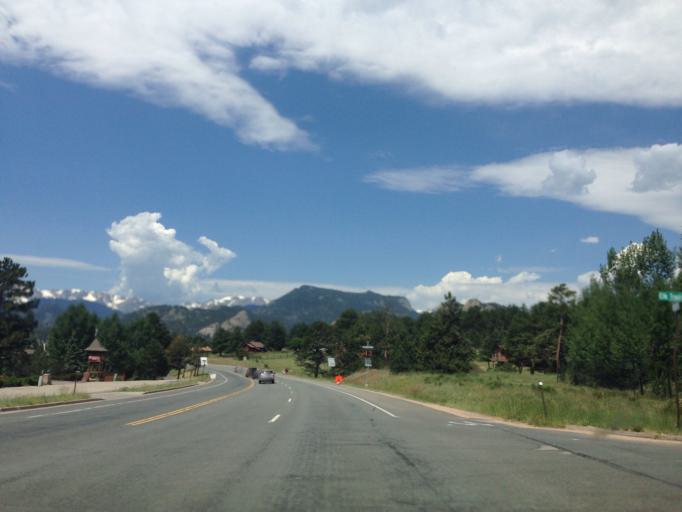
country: US
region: Colorado
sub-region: Larimer County
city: Estes Park
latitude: 40.3839
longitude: -105.5035
